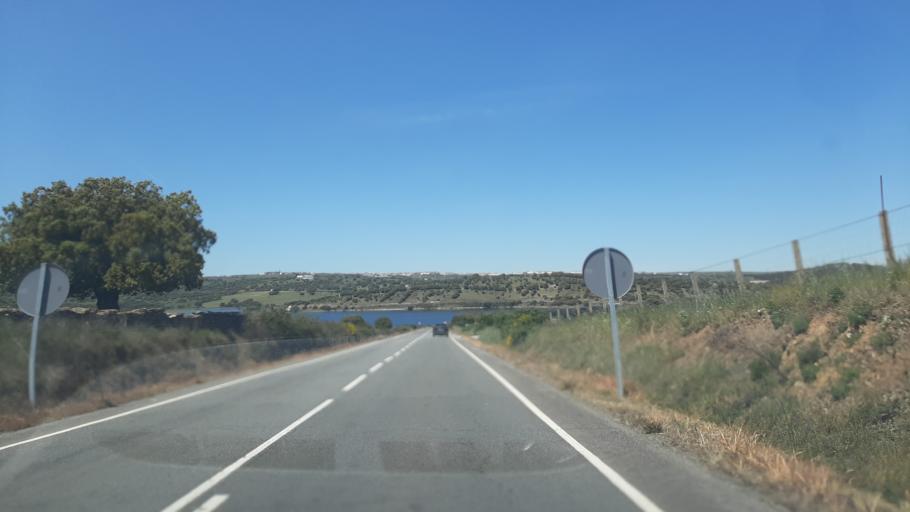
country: ES
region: Castille and Leon
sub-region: Provincia de Salamanca
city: Guijo de Avila
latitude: 40.5493
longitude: -5.6201
